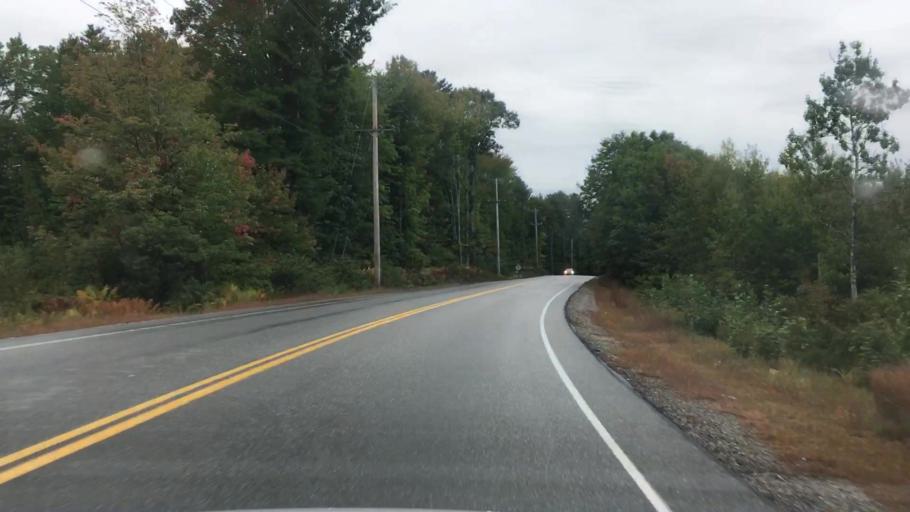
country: US
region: Maine
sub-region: Cumberland County
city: Raymond
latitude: 43.9792
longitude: -70.5291
